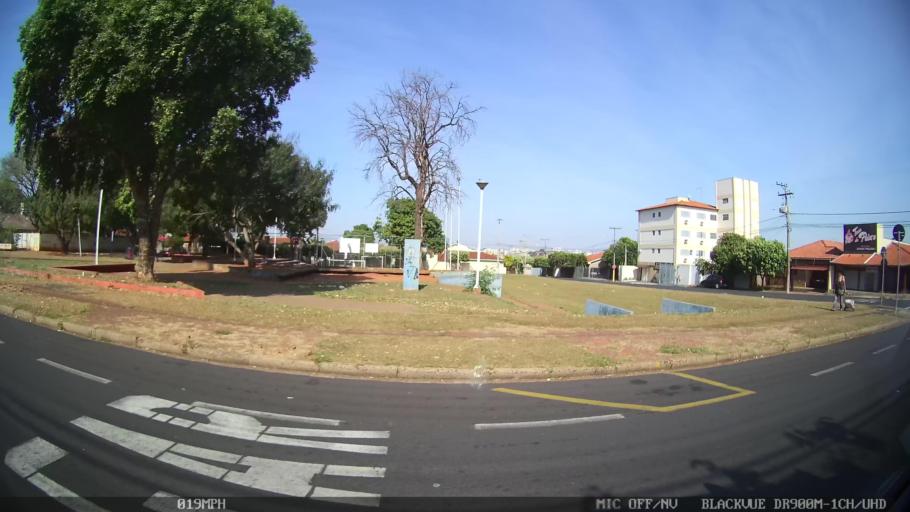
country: BR
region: Sao Paulo
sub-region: Sao Jose Do Rio Preto
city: Sao Jose do Rio Preto
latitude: -20.7968
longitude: -49.4106
